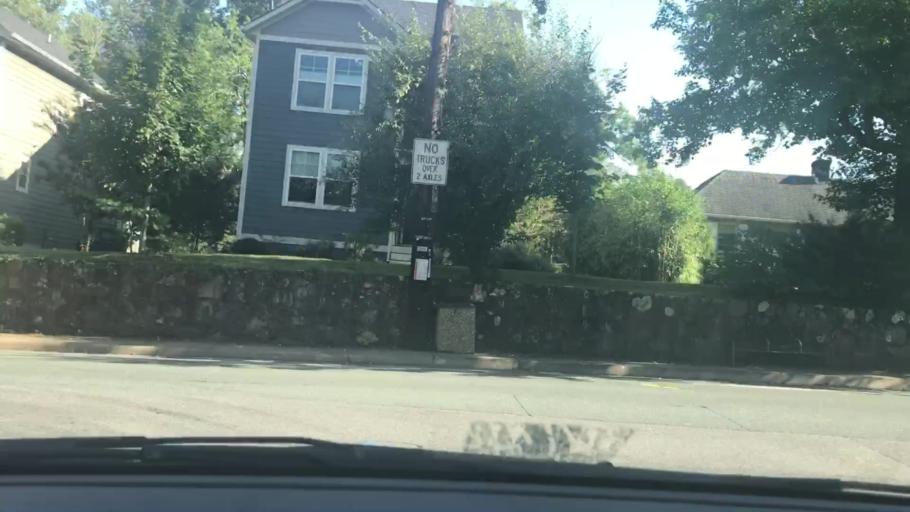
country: US
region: Virginia
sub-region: City of Charlottesville
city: Charlottesville
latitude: 38.0159
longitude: -78.5079
